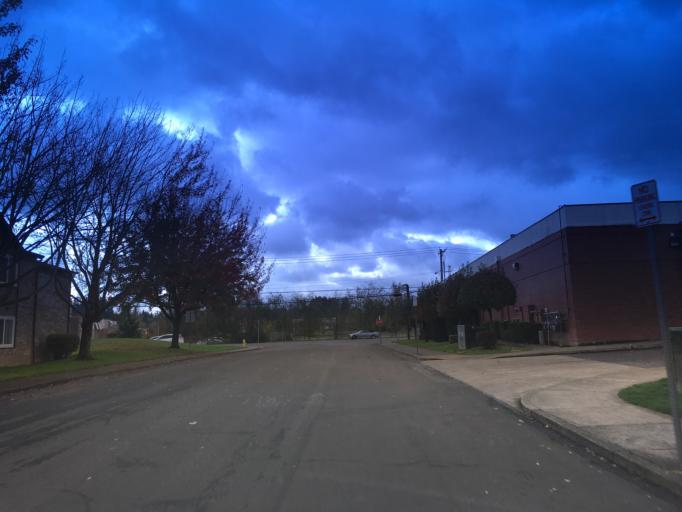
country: US
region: Oregon
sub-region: Multnomah County
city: Fairview
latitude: 45.5364
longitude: -122.4296
